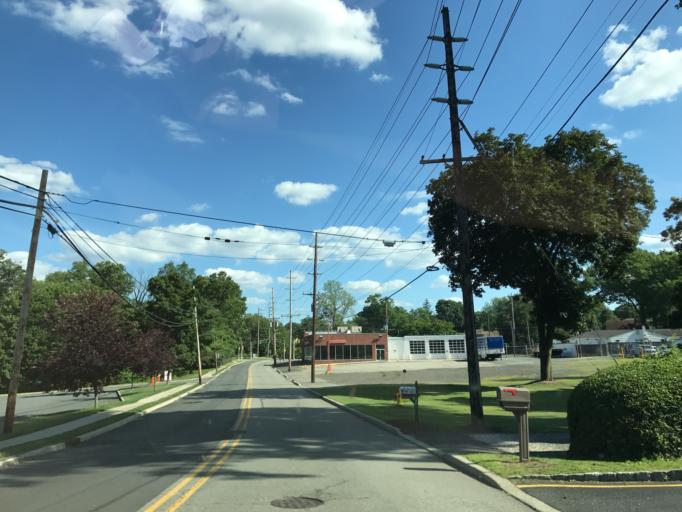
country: US
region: New Jersey
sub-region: Morris County
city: Boonton
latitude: 40.8942
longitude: -74.4168
